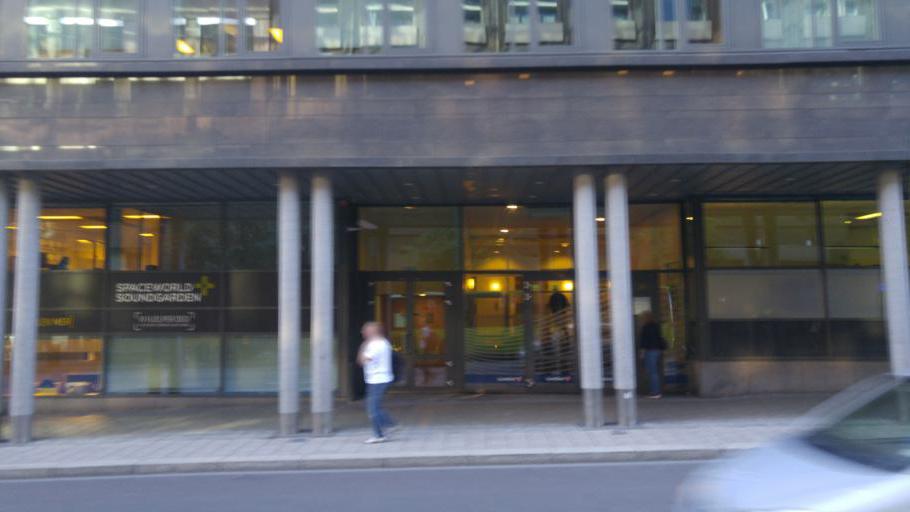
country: NO
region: Oslo
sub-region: Oslo
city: Oslo
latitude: 59.9148
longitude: 10.7522
